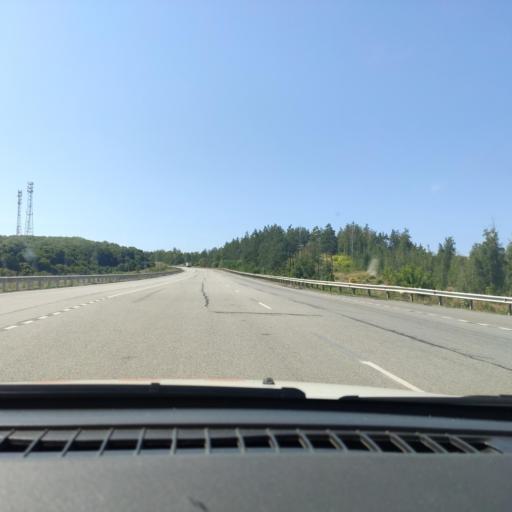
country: RU
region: Voronezj
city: Ostrogozhsk
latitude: 51.0255
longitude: 38.9860
